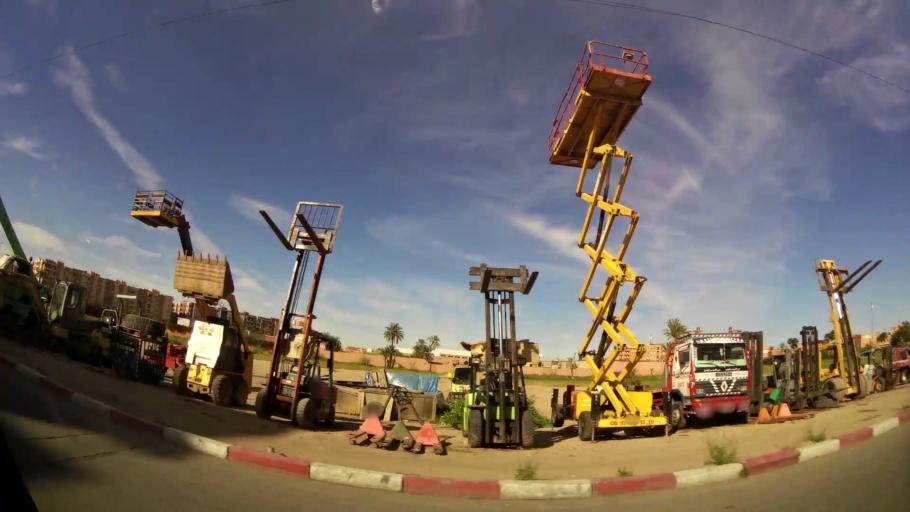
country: MA
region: Marrakech-Tensift-Al Haouz
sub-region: Marrakech
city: Marrakesh
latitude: 31.6559
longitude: -8.0208
